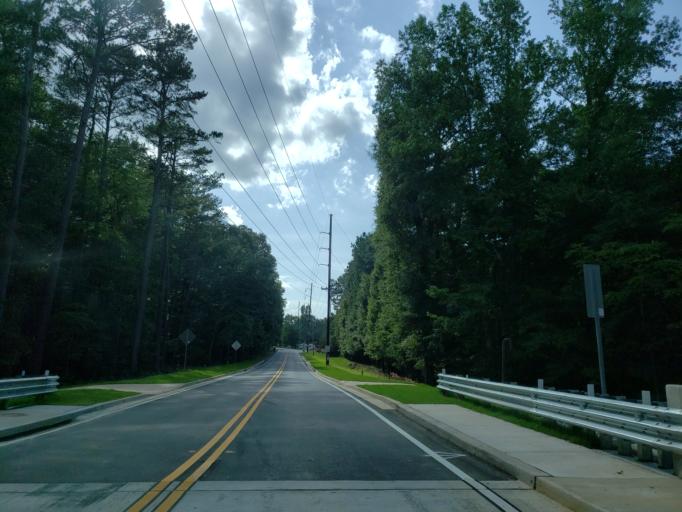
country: US
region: Georgia
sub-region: Cobb County
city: Powder Springs
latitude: 33.8753
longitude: -84.6434
